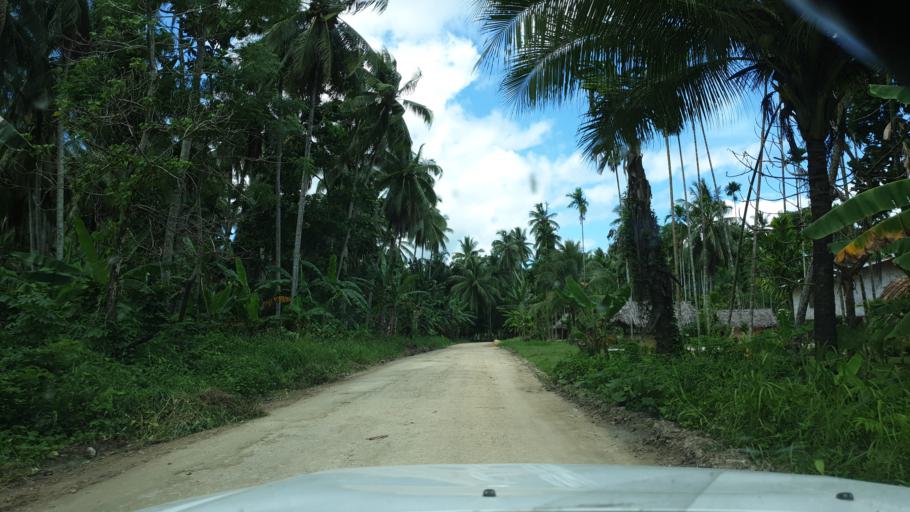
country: PG
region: East Sepik
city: Angoram
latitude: -4.2316
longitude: 144.9361
